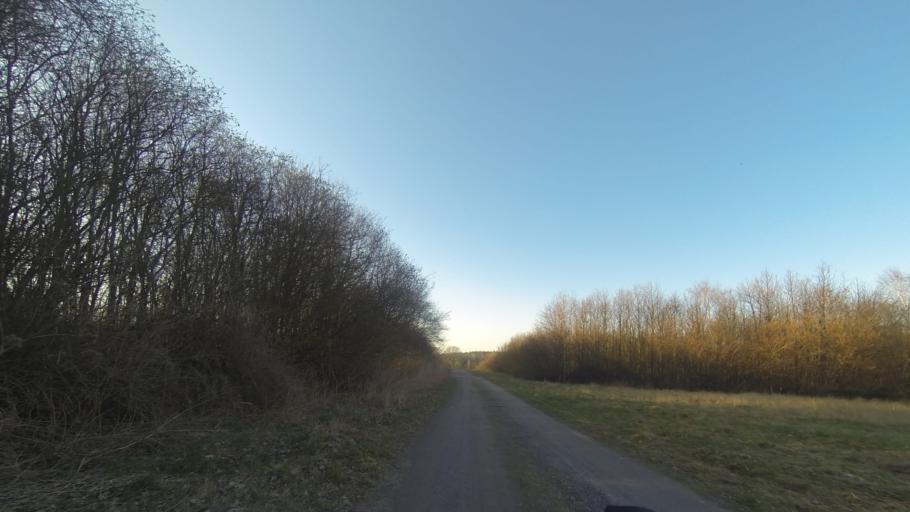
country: DE
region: Saxony
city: Albertstadt
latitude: 51.1329
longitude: 13.7603
